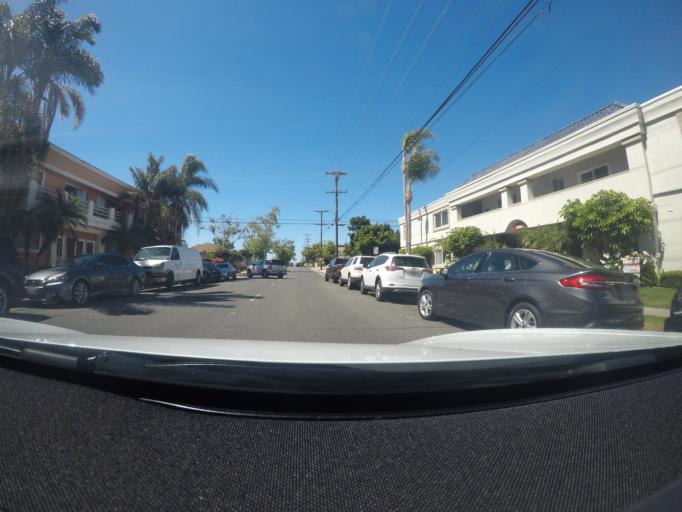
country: US
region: California
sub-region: Los Angeles County
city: Redondo Beach
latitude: 33.8392
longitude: -118.3667
